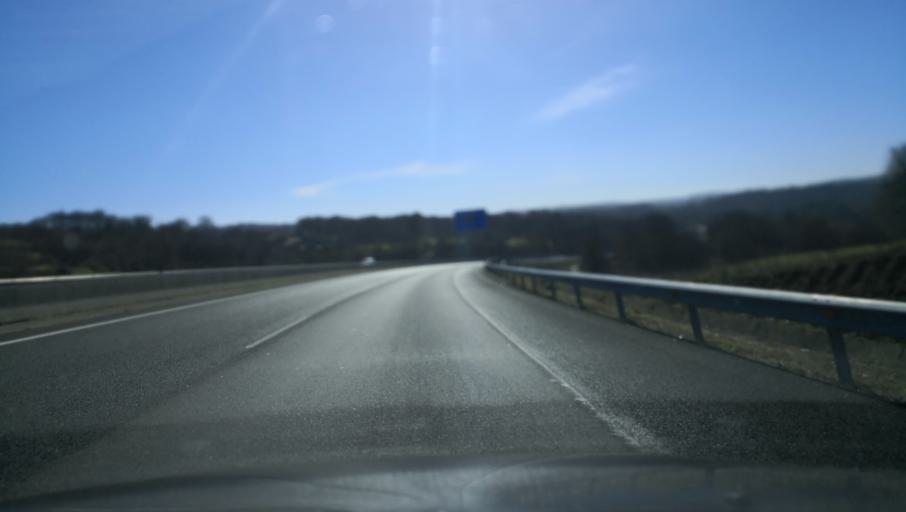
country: ES
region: Galicia
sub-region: Provincia de Pontevedra
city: Lalin
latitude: 42.6480
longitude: -8.1341
